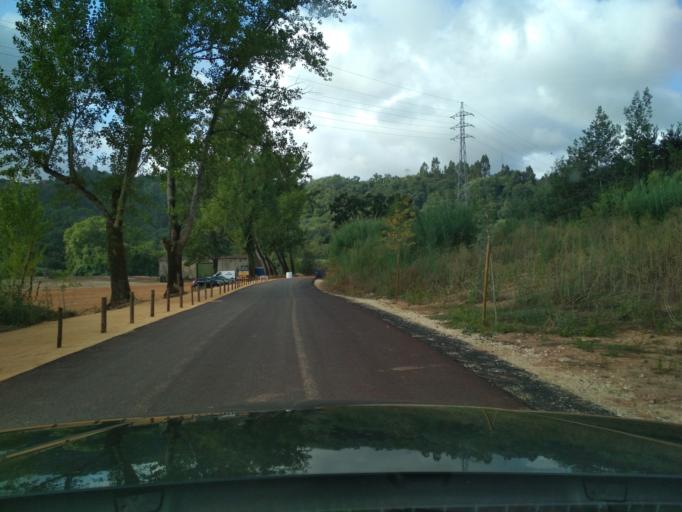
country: PT
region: Coimbra
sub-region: Coimbra
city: Coimbra
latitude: 40.1810
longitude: -8.4164
